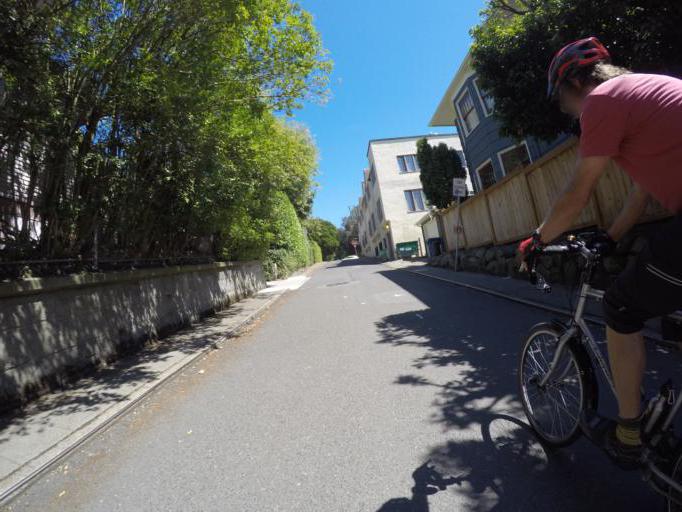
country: US
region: Washington
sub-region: King County
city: Seattle
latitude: 47.6253
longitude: -122.3178
